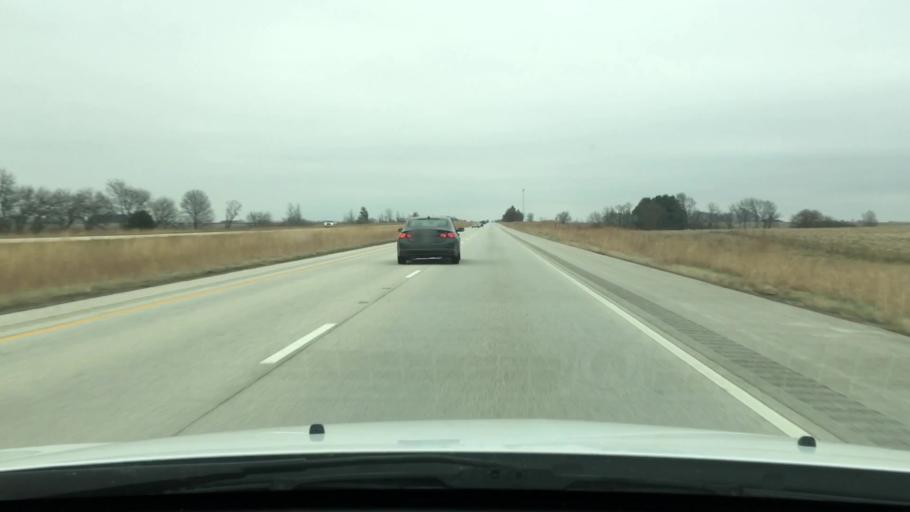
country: US
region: Illinois
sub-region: Sangamon County
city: New Berlin
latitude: 39.7404
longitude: -89.8893
